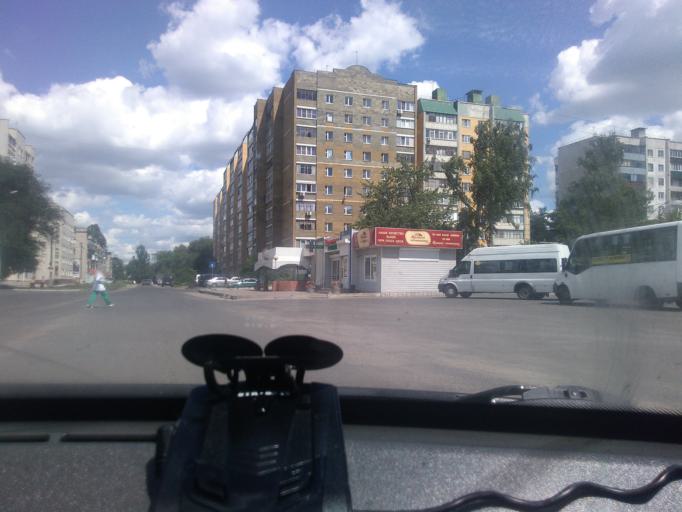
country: RU
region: Kursk
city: Voroshnevo
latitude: 51.6675
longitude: 36.0698
